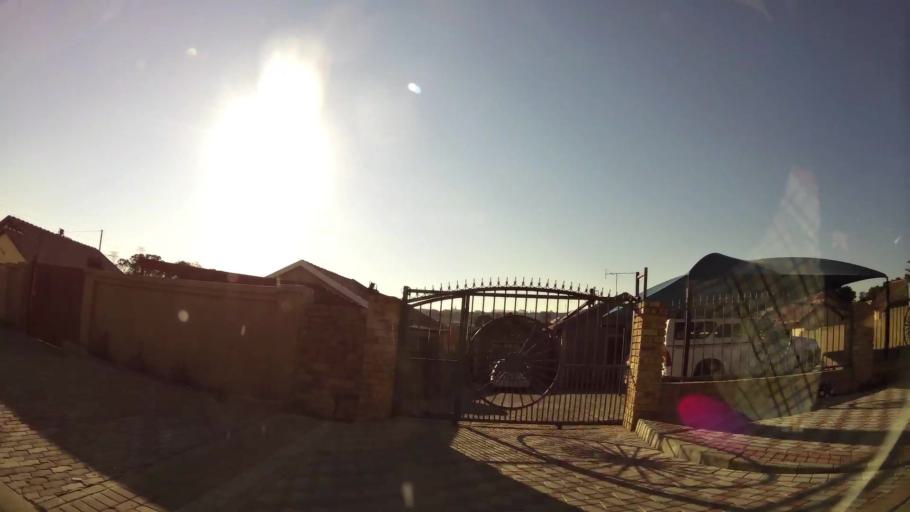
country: ZA
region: Gauteng
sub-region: City of Johannesburg Metropolitan Municipality
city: Modderfontein
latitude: -26.0422
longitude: 28.1534
